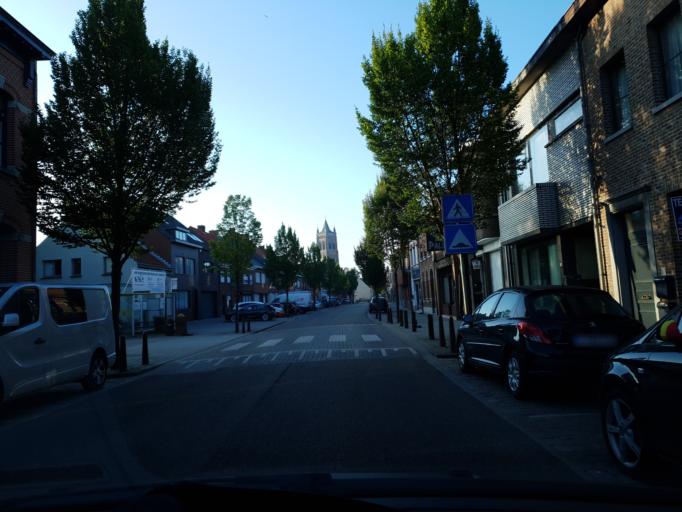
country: BE
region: Flanders
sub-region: Provincie Antwerpen
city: Brecht
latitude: 51.3491
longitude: 4.6764
